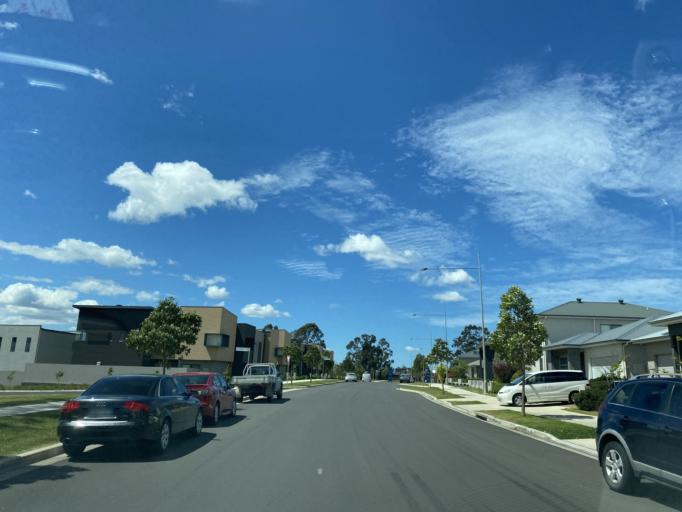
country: AU
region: New South Wales
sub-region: Camden
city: Narellan
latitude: -34.0138
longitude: 150.7773
